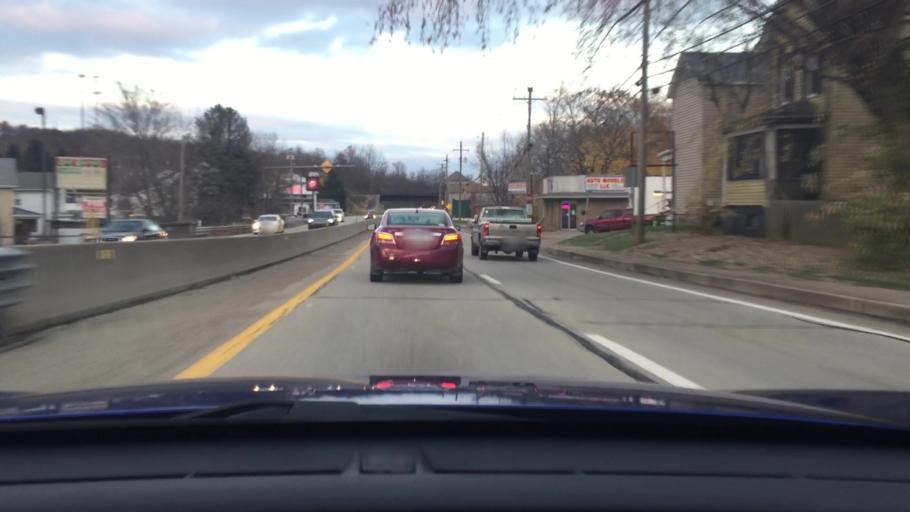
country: US
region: Pennsylvania
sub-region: Westmoreland County
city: South Greensburg
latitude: 40.2753
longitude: -79.5549
